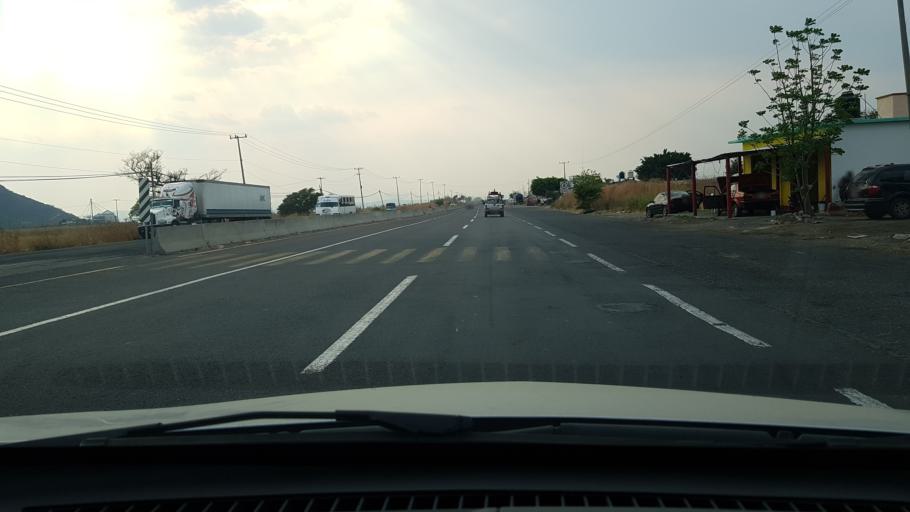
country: MX
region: Morelos
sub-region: Ayala
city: Unidad Habitacional Mariano Matamoros
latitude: 18.7524
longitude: -98.8547
